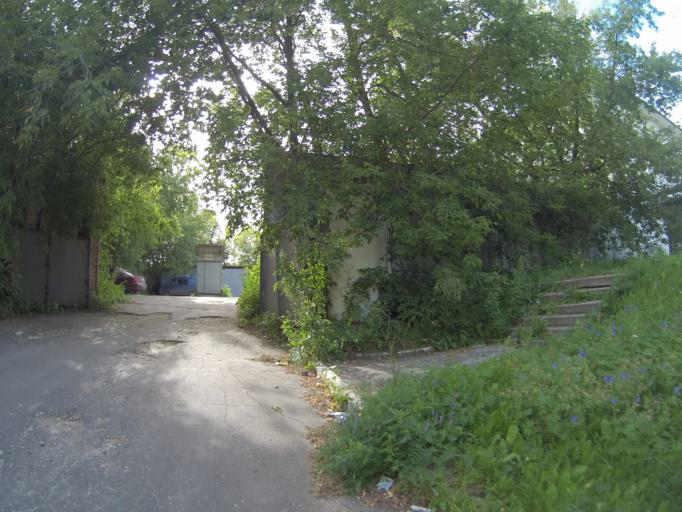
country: RU
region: Vladimir
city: Kommunar
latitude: 56.1498
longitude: 40.4364
